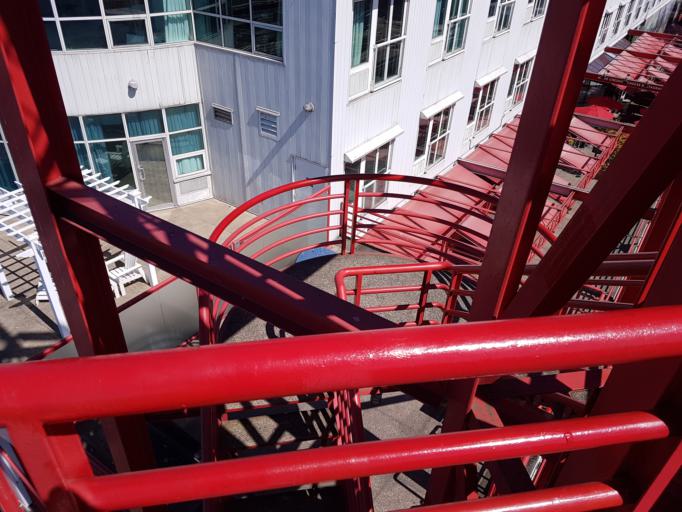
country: CA
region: British Columbia
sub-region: Fraser Valley Regional District
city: North Vancouver
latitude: 49.3099
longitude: -123.0822
